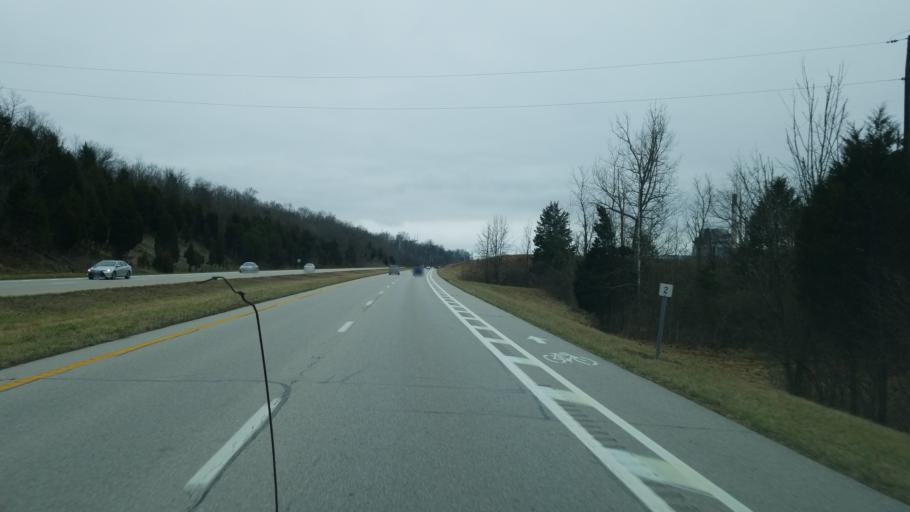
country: US
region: Ohio
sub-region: Clermont County
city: New Richmond
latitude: 39.0034
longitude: -84.2981
